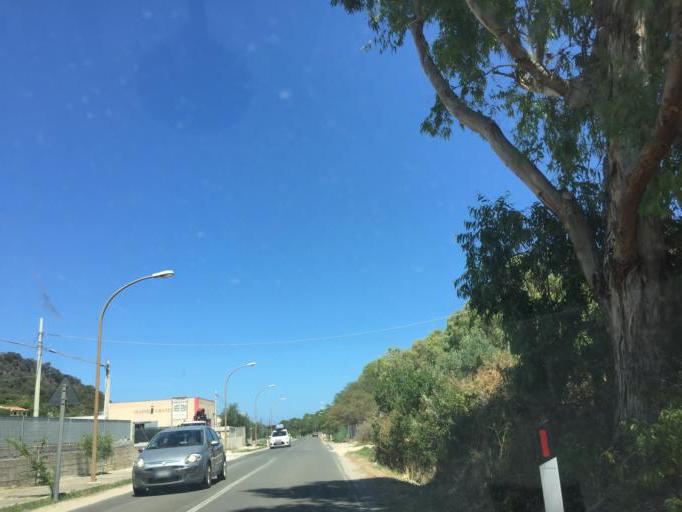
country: IT
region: Sardinia
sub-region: Provincia di Sassari
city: Castelsardo
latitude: 40.8954
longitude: 8.7438
